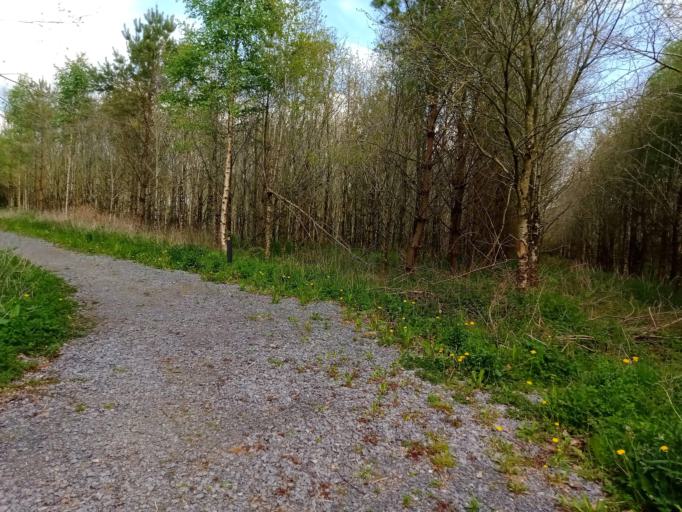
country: IE
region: Leinster
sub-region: Kilkenny
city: Ballyragget
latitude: 52.7267
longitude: -7.4142
